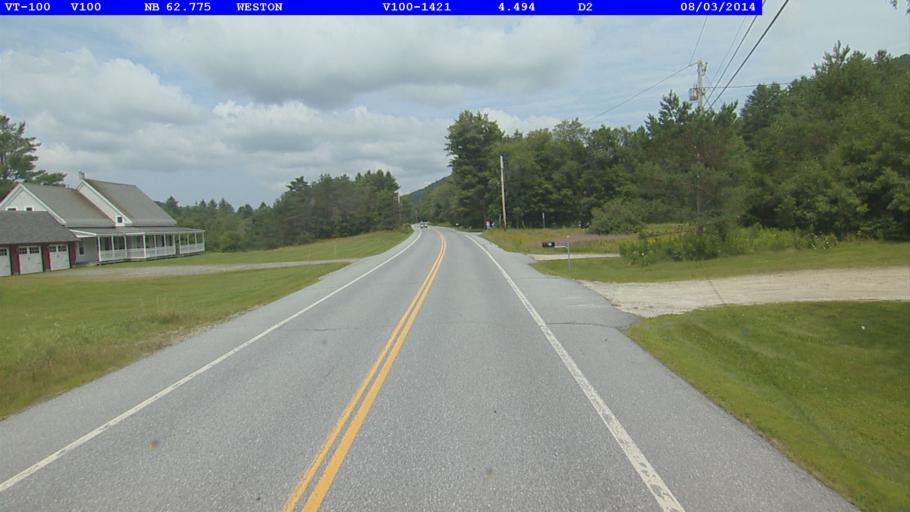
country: US
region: Vermont
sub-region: Windsor County
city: Chester
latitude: 43.3089
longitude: -72.7868
